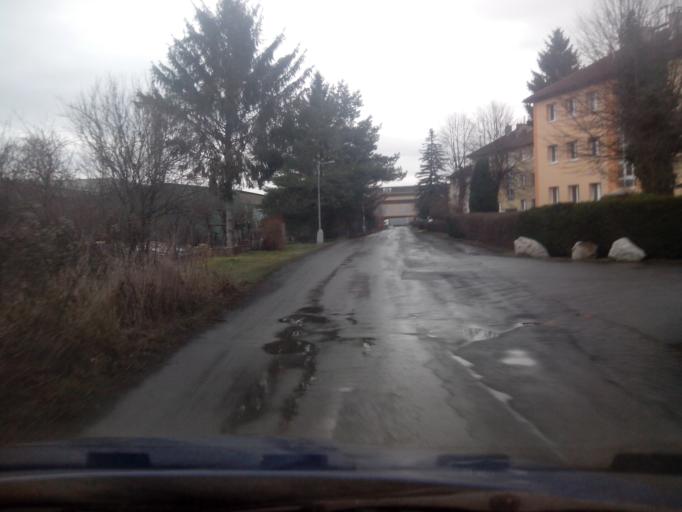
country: CZ
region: Central Bohemia
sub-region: Okres Beroun
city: Kraluv Dvur
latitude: 49.9360
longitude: 14.0293
